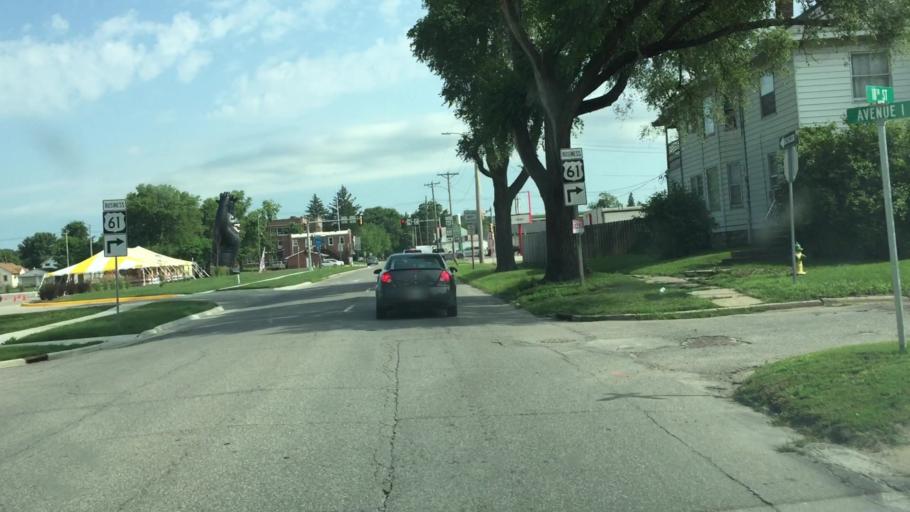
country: US
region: Iowa
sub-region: Lee County
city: Fort Madison
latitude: 40.6291
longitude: -91.3302
